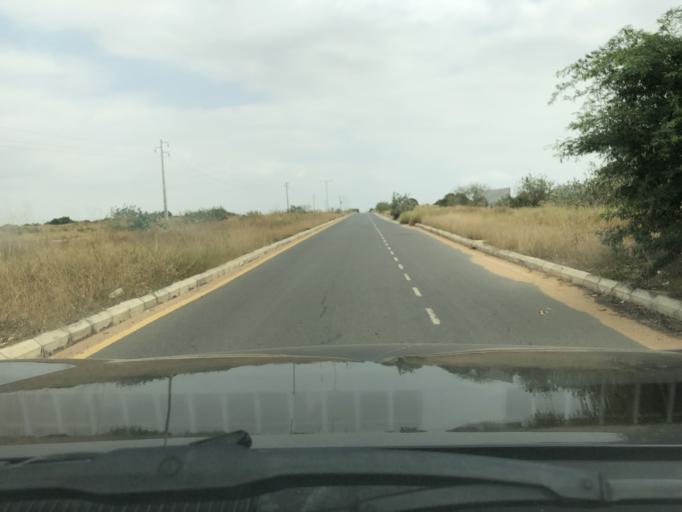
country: AO
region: Luanda
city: Luanda
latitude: -8.9546
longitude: 13.2536
